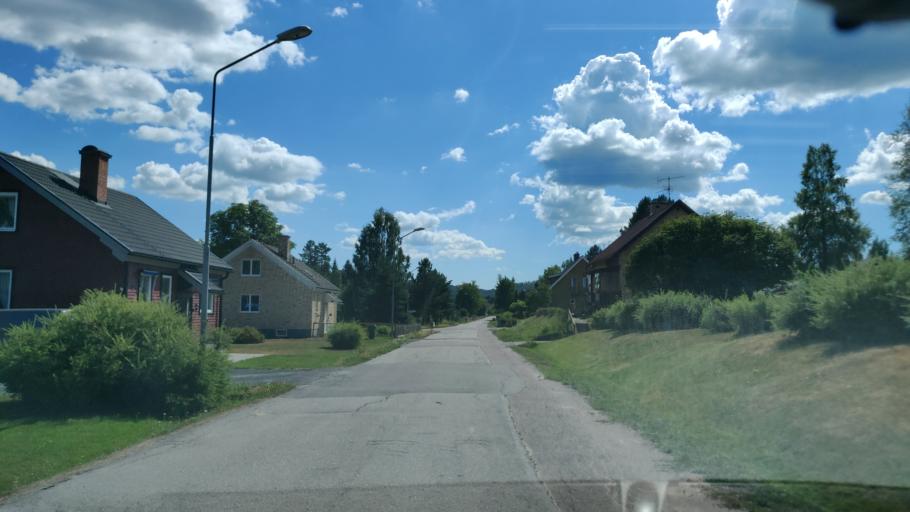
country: SE
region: Vaermland
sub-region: Hagfors Kommun
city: Ekshaerad
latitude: 60.1792
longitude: 13.4937
